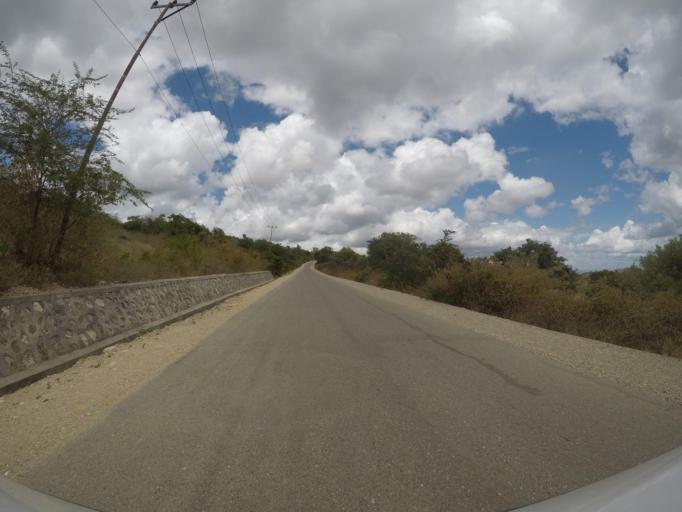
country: TL
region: Lautem
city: Lospalos
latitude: -8.3654
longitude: 126.9287
